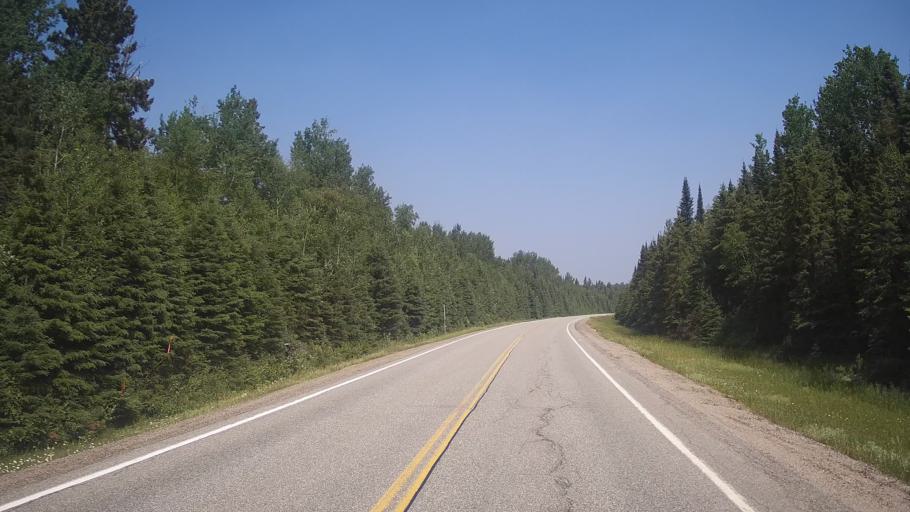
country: CA
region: Ontario
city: Timmins
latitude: 48.0815
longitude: -81.5965
